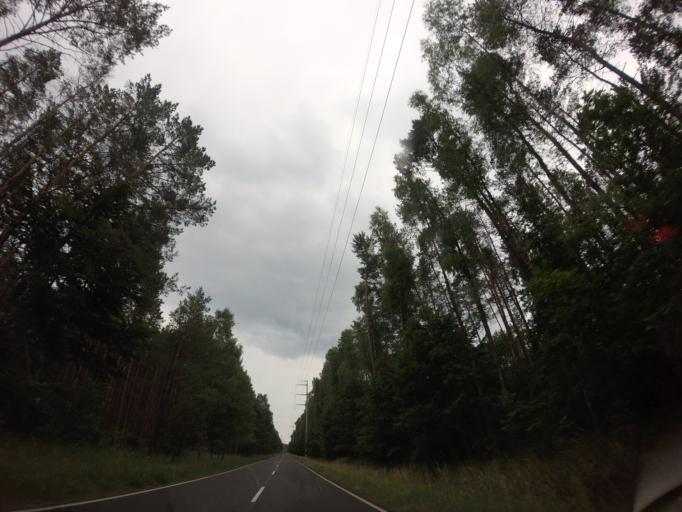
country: PL
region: West Pomeranian Voivodeship
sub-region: Powiat drawski
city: Czaplinek
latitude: 53.4918
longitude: 16.2261
